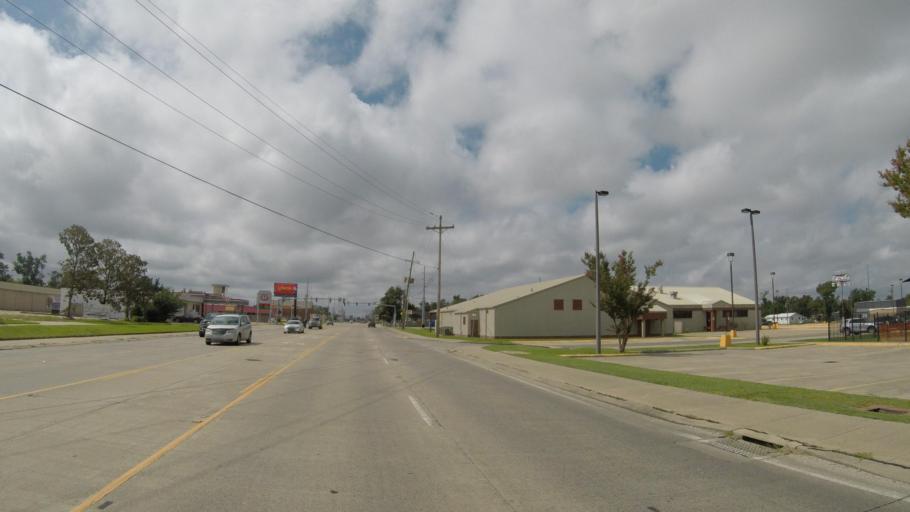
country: US
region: Louisiana
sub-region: Calcasieu Parish
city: Westlake
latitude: 30.2490
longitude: -93.2581
